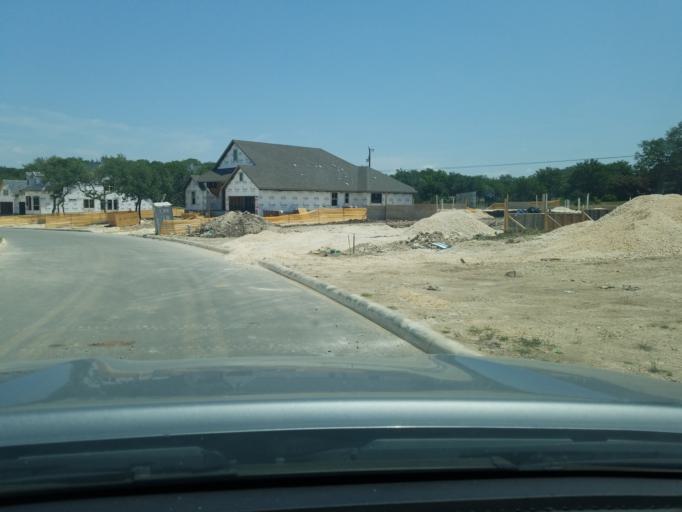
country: US
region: Texas
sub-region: Bexar County
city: Timberwood Park
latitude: 29.7126
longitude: -98.5034
